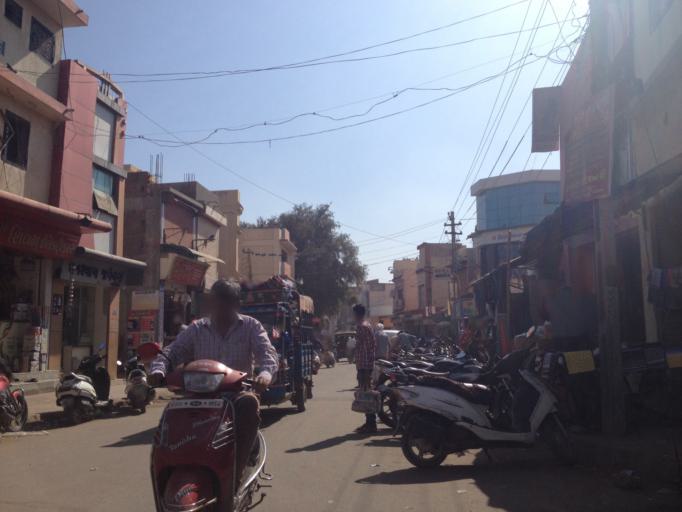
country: IN
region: Gujarat
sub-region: Kachchh
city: Anjar
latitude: 23.1134
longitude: 70.0279
